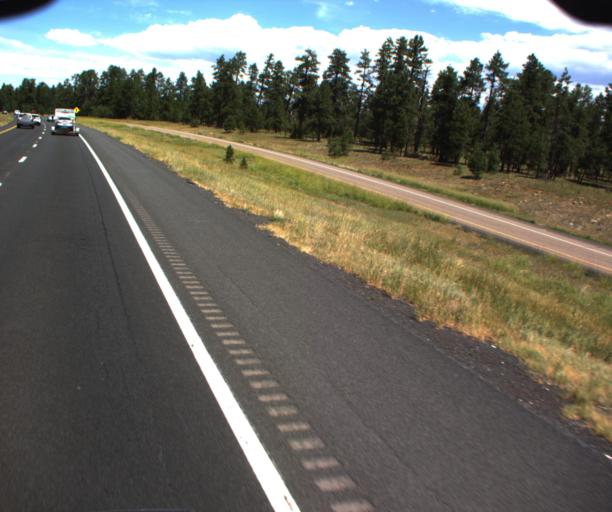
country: US
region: Arizona
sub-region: Coconino County
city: Sedona
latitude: 34.8537
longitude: -111.6072
